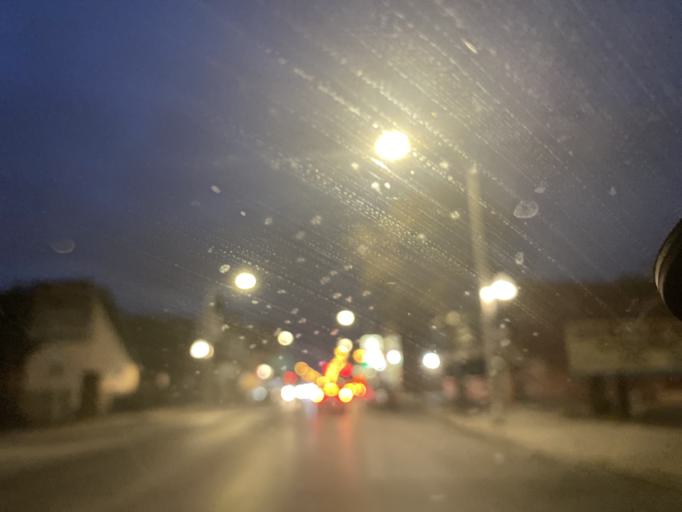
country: US
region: Illinois
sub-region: Cook County
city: Chicago
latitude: 41.7796
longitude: -87.6514
